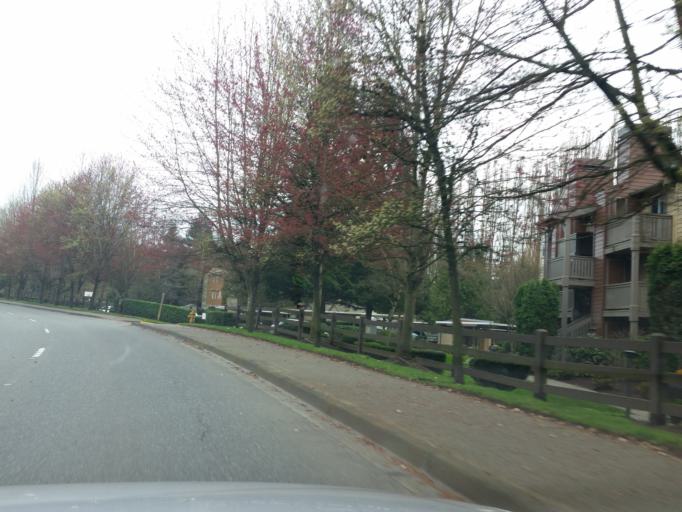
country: US
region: Washington
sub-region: King County
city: Woodinville
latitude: 47.7520
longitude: -122.1652
